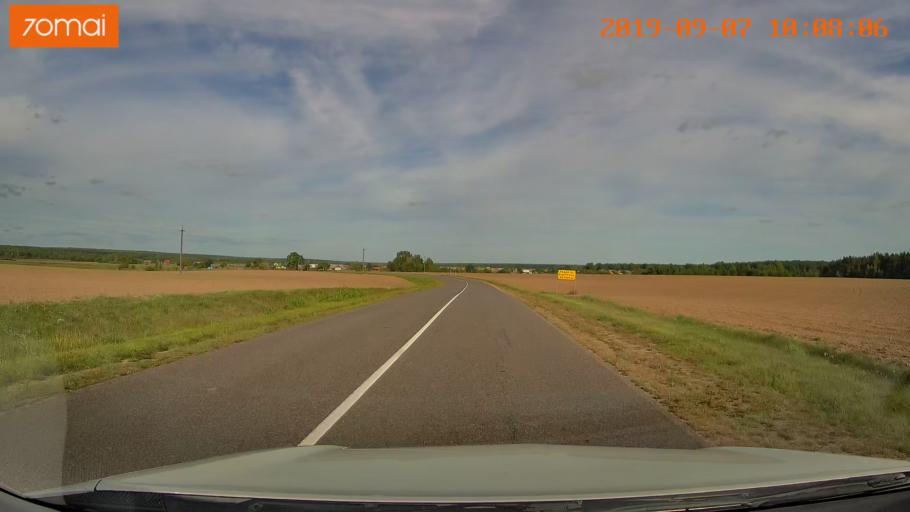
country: BY
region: Grodnenskaya
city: Voranava
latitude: 54.0838
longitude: 25.3920
